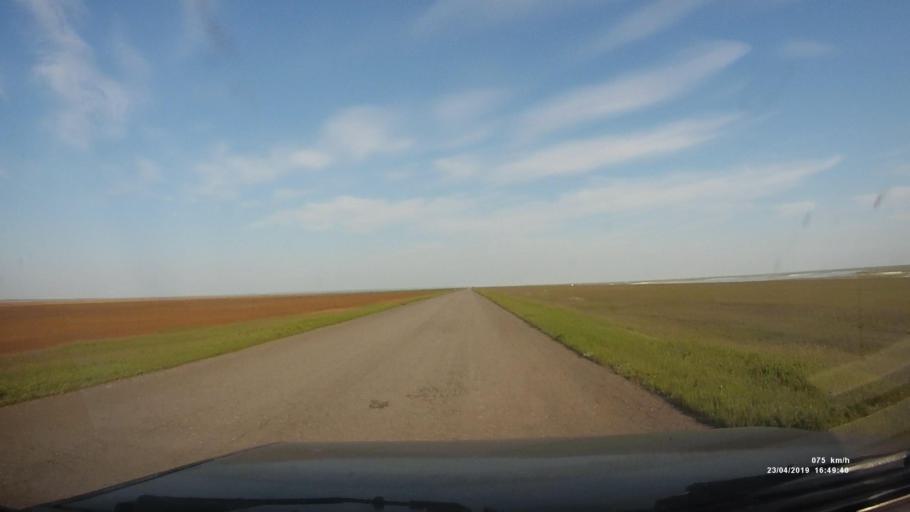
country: RU
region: Kalmykiya
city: Priyutnoye
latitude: 46.3301
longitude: 43.2801
